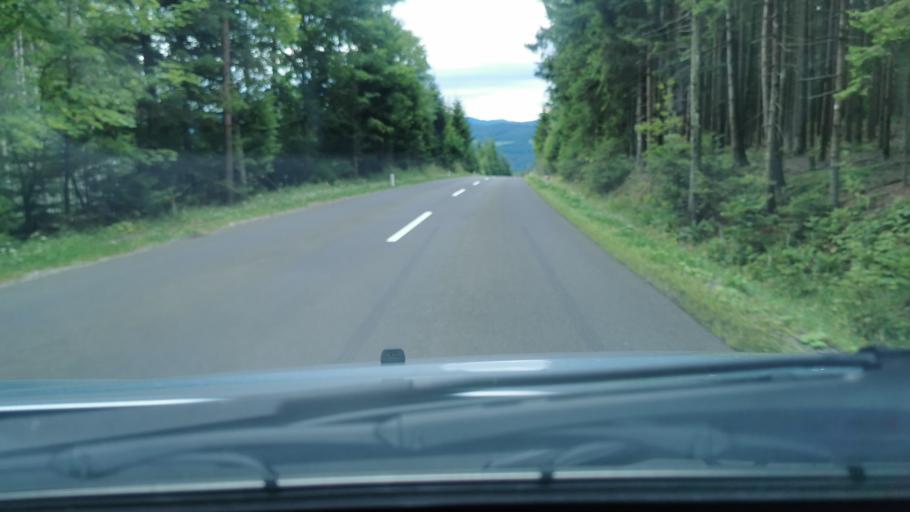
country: AT
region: Styria
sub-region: Politischer Bezirk Weiz
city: Fischbach
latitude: 47.4092
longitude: 15.6600
